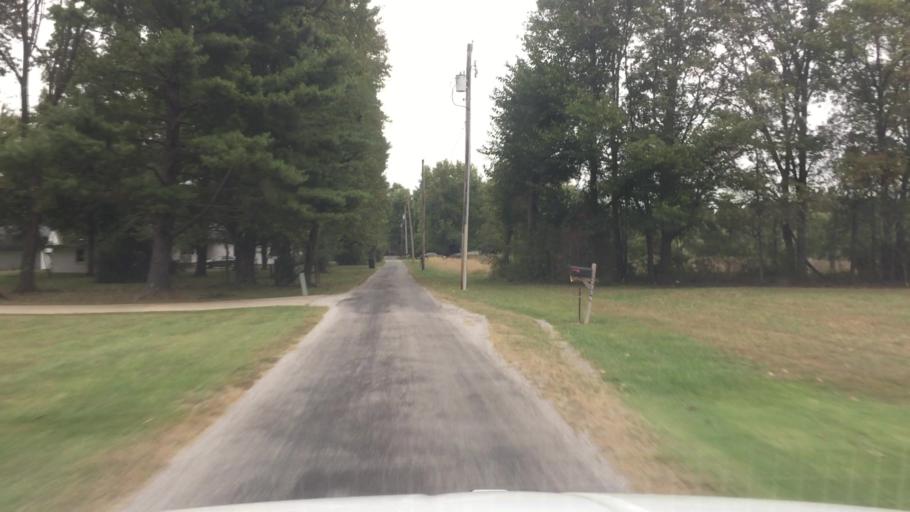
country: US
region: Illinois
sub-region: Franklin County
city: West Frankfort
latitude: 37.8965
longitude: -88.9720
